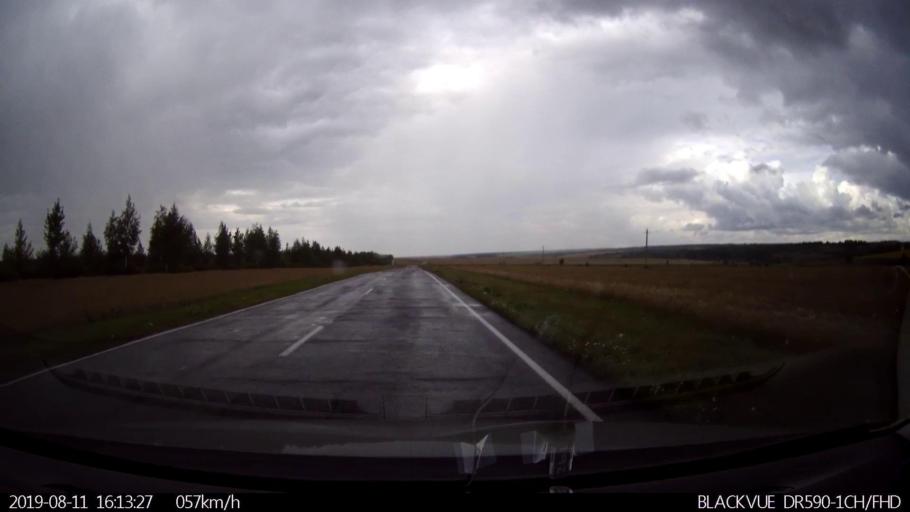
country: RU
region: Ulyanovsk
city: Ignatovka
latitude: 54.0203
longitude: 47.6368
